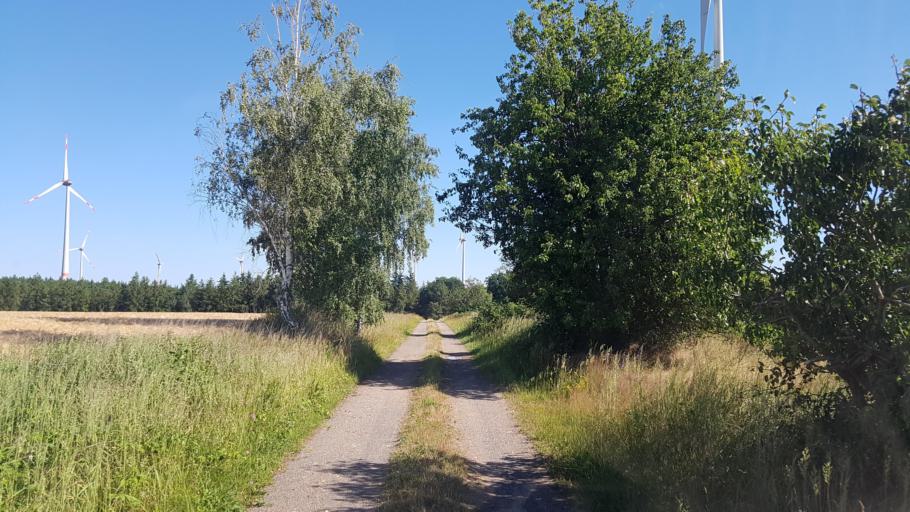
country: DE
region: Brandenburg
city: Treuenbrietzen
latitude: 52.0079
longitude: 12.8571
